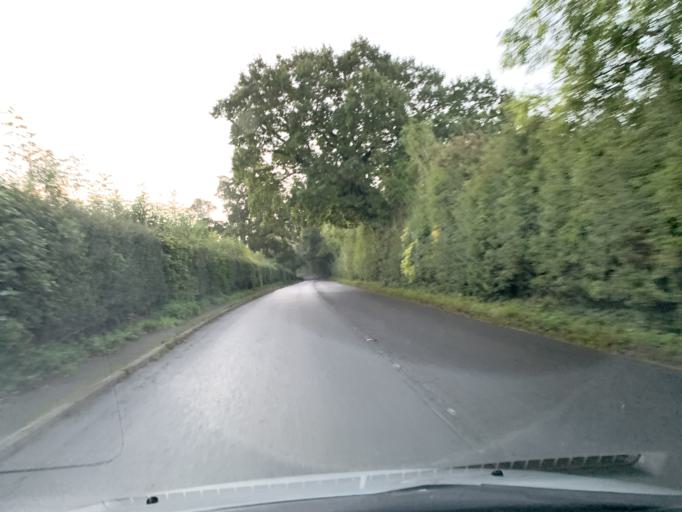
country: GB
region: England
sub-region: Wiltshire
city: Alderbury
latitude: 51.0508
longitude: -1.7502
